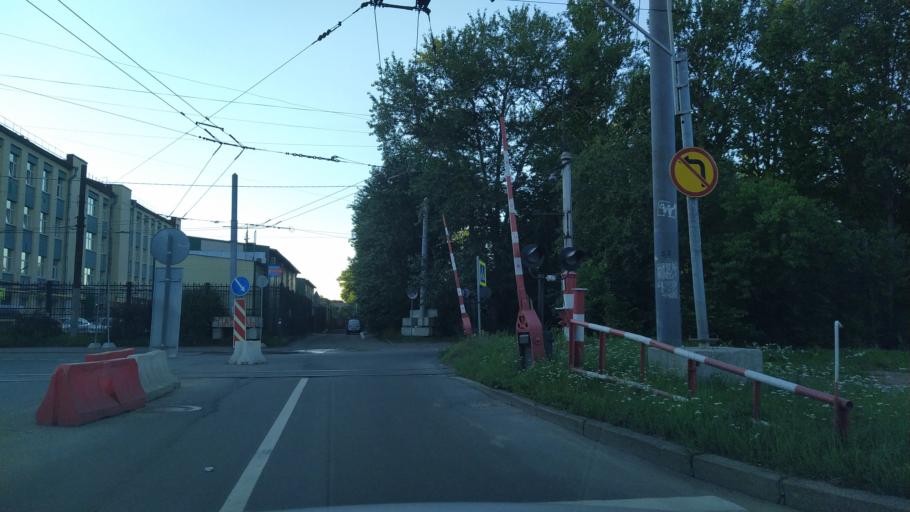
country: RU
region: Leningrad
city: Finlyandskiy
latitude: 59.9704
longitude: 30.3650
